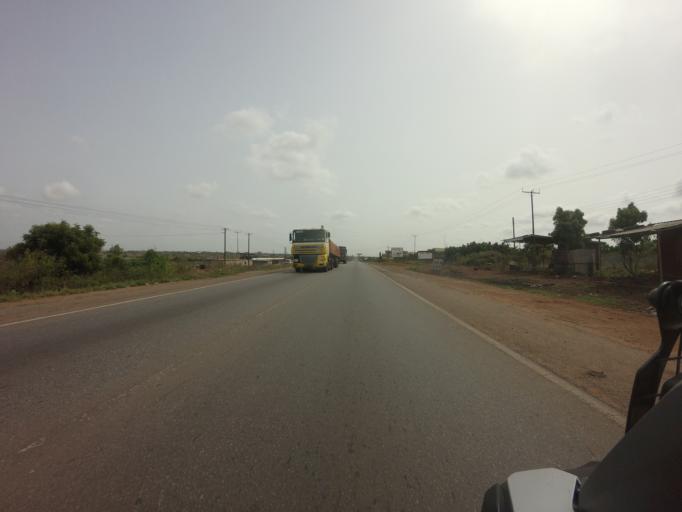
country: GH
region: Greater Accra
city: Tema
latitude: 5.7720
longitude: 0.0735
